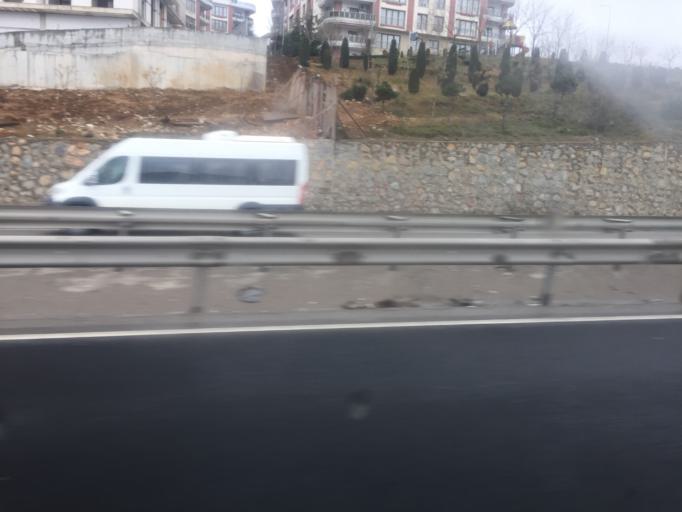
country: TR
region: Kocaeli
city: Gebze
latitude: 40.7879
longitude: 29.4255
